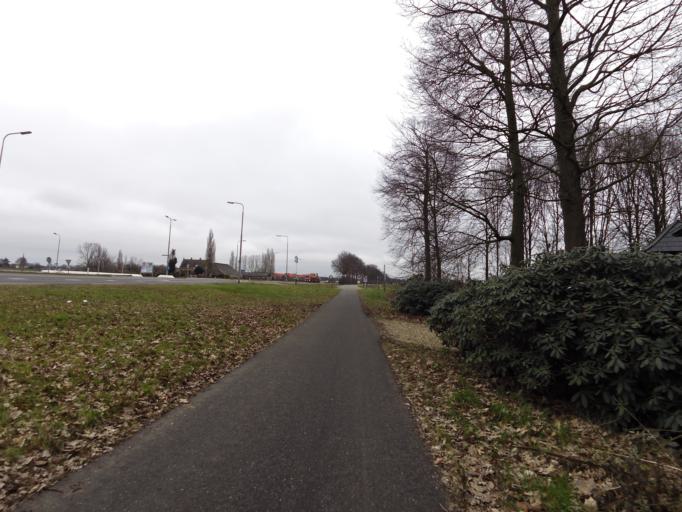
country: NL
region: Gelderland
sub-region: Gemeente Doesburg
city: Doesburg
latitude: 51.9967
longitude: 6.1136
